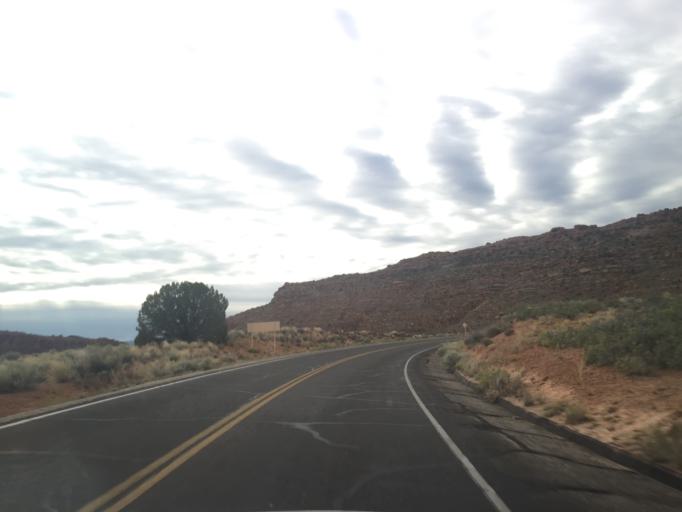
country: US
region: Utah
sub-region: Grand County
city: Moab
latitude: 38.7281
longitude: -109.5396
